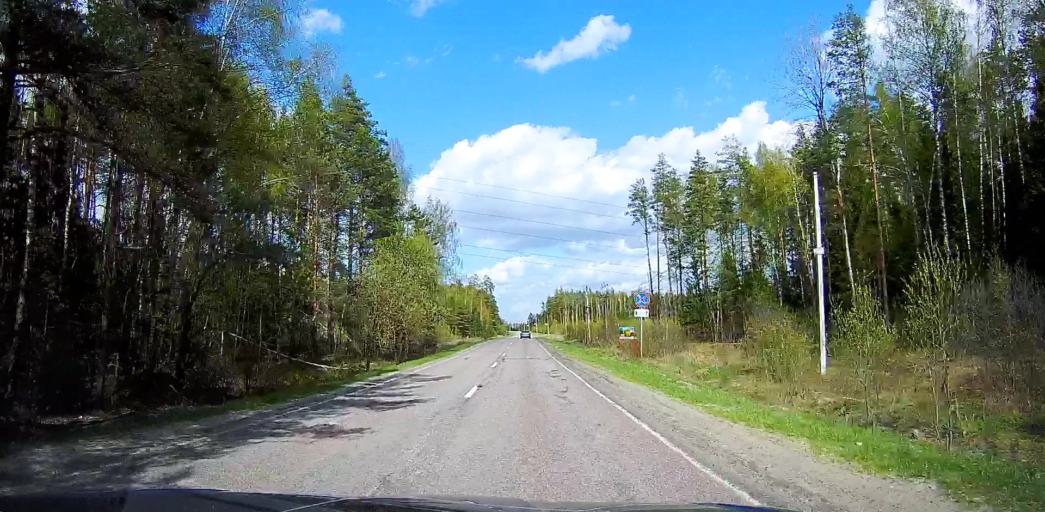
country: RU
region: Moskovskaya
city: Davydovo
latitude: 55.5930
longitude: 38.8351
